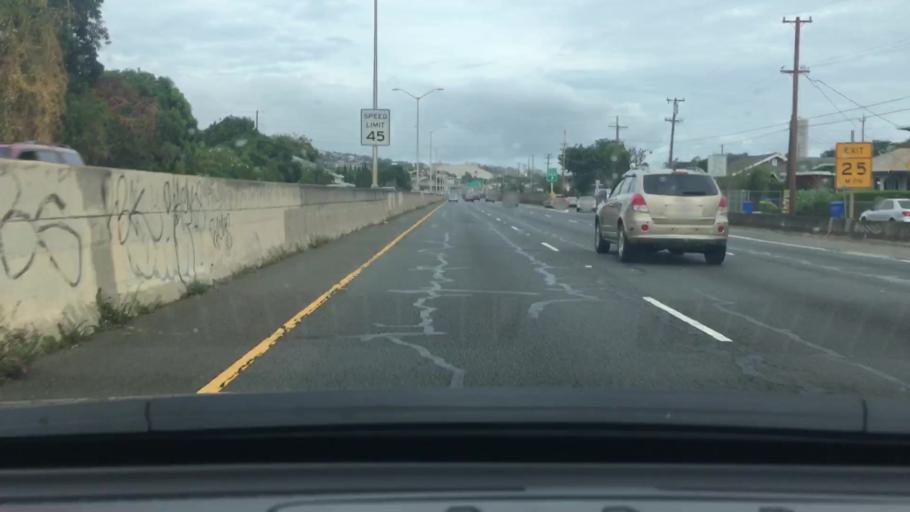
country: US
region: Hawaii
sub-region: Honolulu County
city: Honolulu
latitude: 21.2980
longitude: -157.8288
